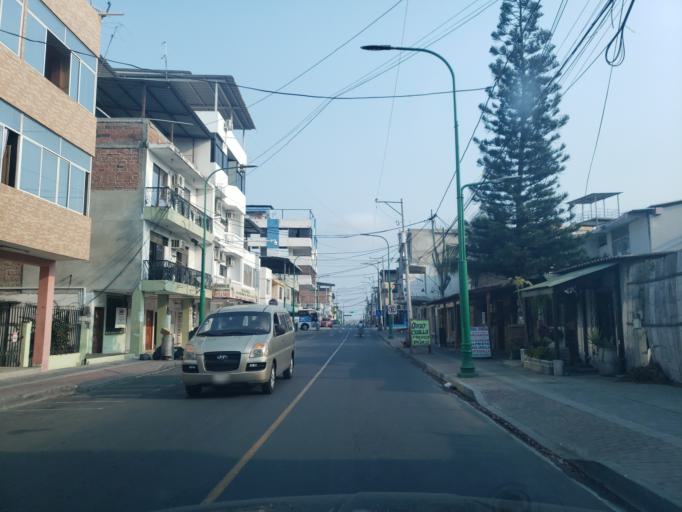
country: EC
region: Manabi
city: Manta
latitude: -0.9525
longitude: -80.7290
